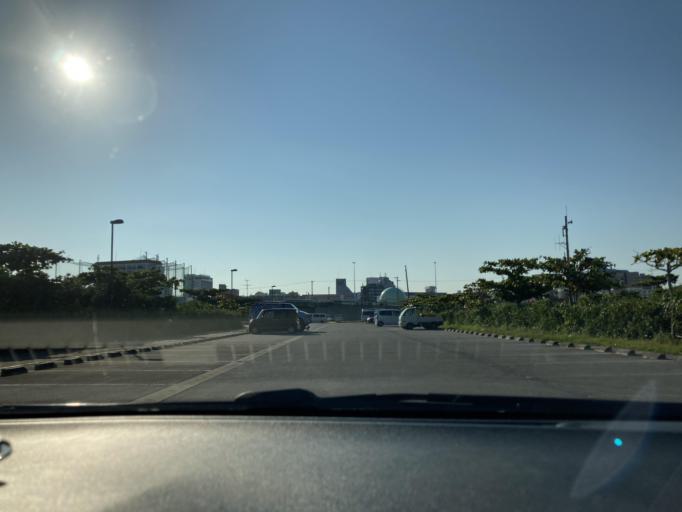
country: JP
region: Okinawa
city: Naha-shi
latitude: 26.2206
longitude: 127.6639
